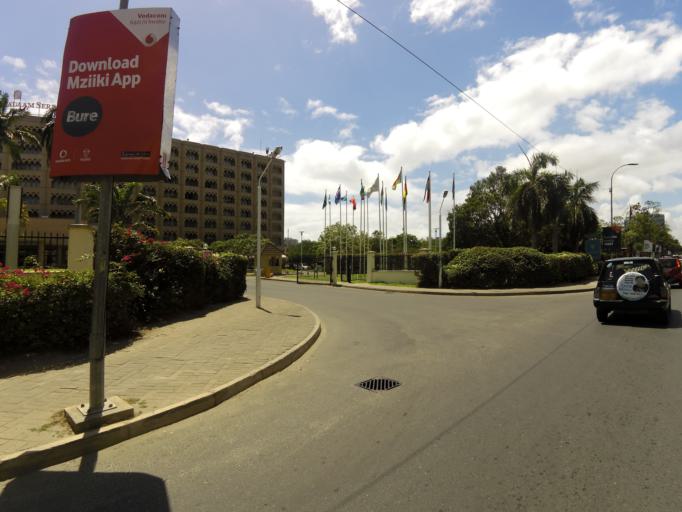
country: TZ
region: Dar es Salaam
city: Dar es Salaam
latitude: -6.8111
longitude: 39.2875
